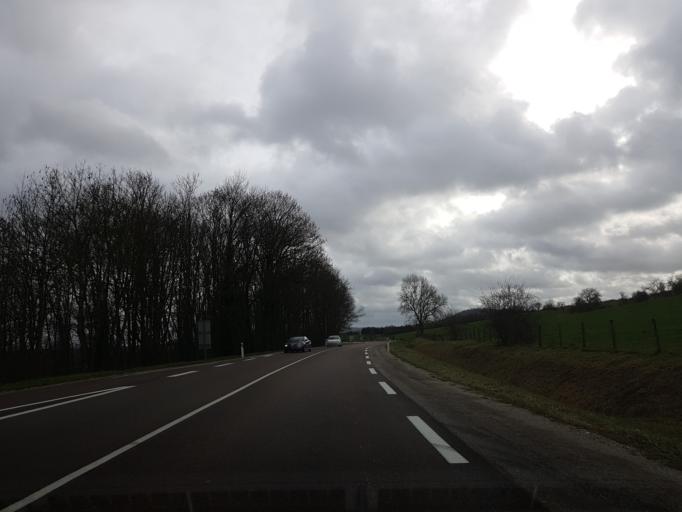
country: FR
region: Champagne-Ardenne
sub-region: Departement de la Haute-Marne
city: Rolampont
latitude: 47.9118
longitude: 5.2910
